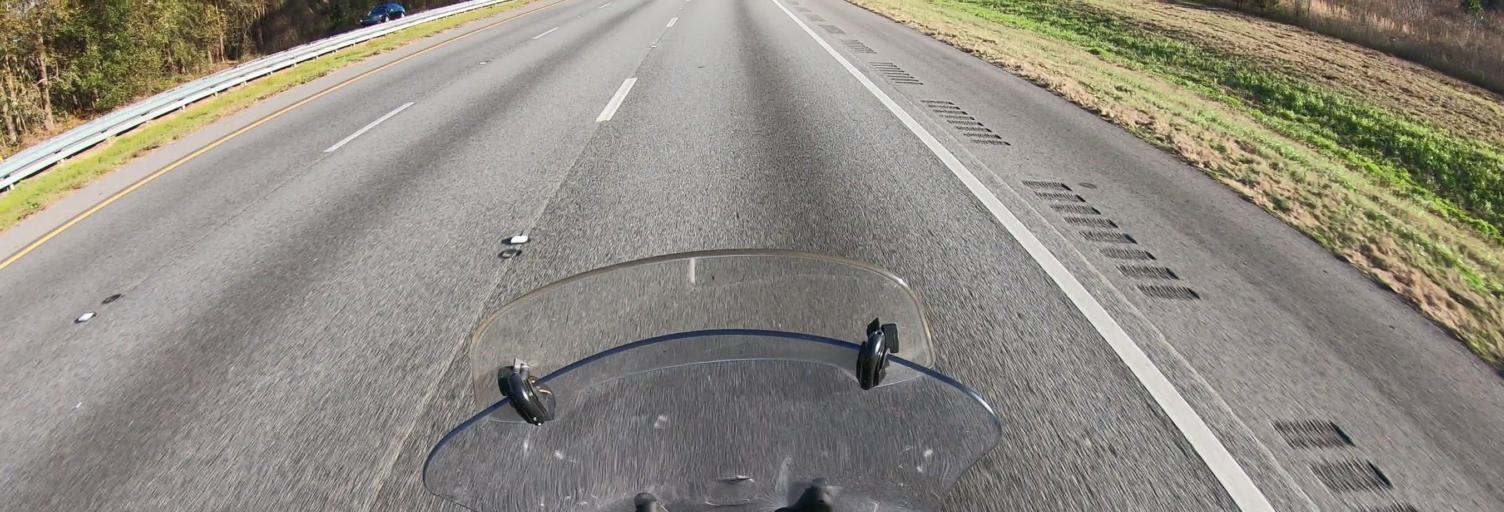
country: US
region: Florida
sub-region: Alachua County
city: Alachua
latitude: 29.7576
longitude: -82.4990
